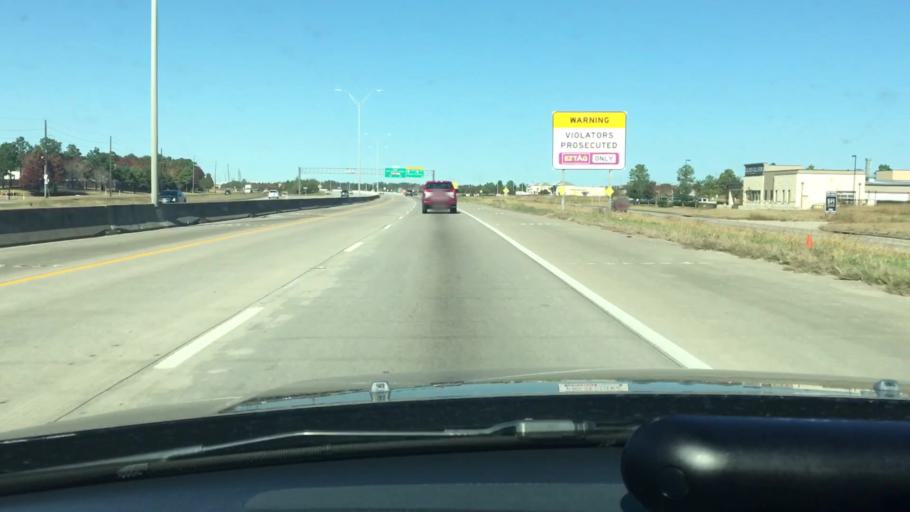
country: US
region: Texas
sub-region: Harris County
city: Cloverleaf
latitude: 29.8200
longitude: -95.1657
